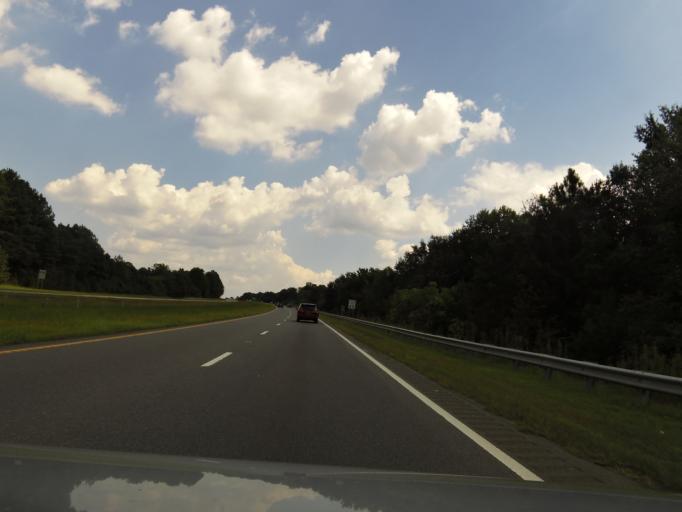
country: US
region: North Carolina
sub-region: Cleveland County
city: Kings Mountain
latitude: 35.2542
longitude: -81.3523
